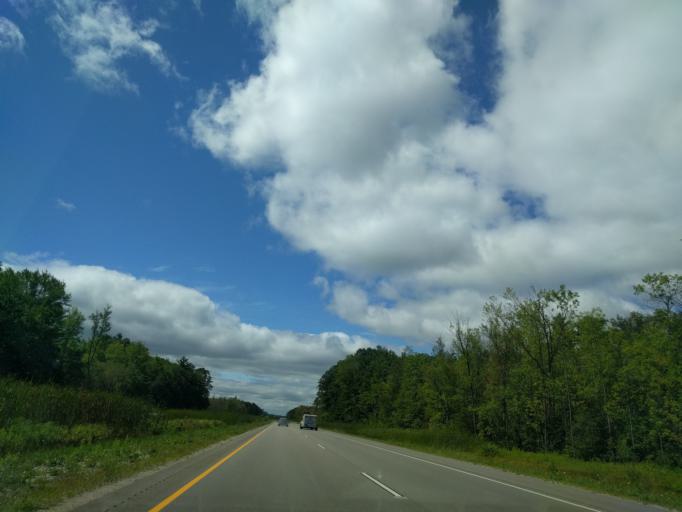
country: US
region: Wisconsin
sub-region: Oconto County
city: Oconto
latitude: 44.8134
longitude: -87.9527
